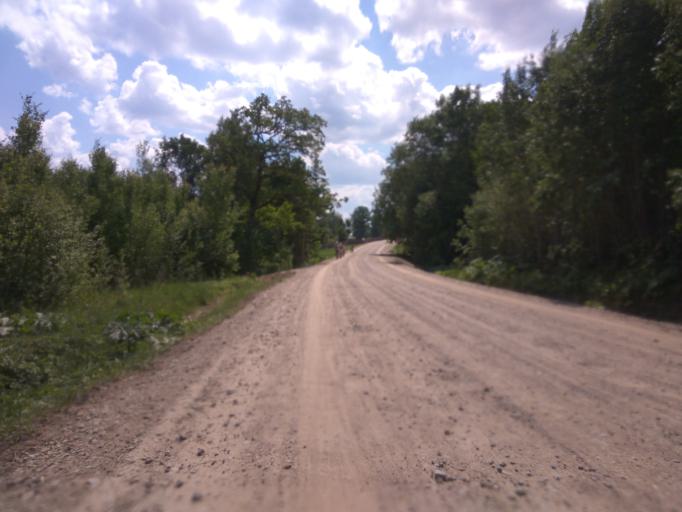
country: LV
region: Kuldigas Rajons
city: Kuldiga
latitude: 56.9062
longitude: 21.9645
